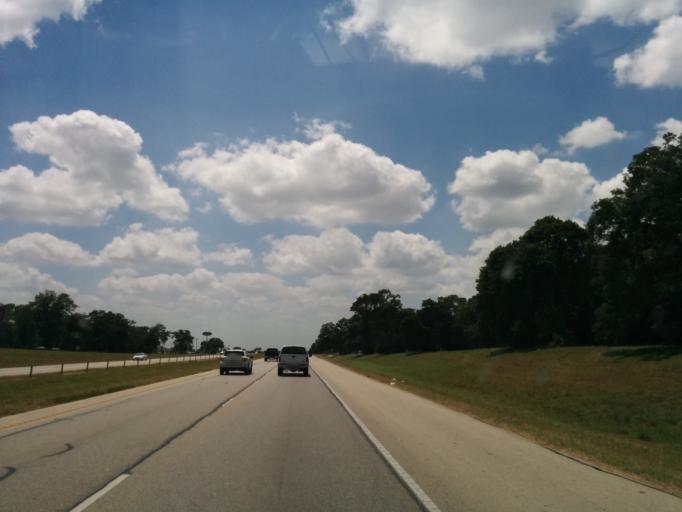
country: US
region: Texas
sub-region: Bastrop County
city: Wyldwood
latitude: 30.1109
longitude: -97.3995
